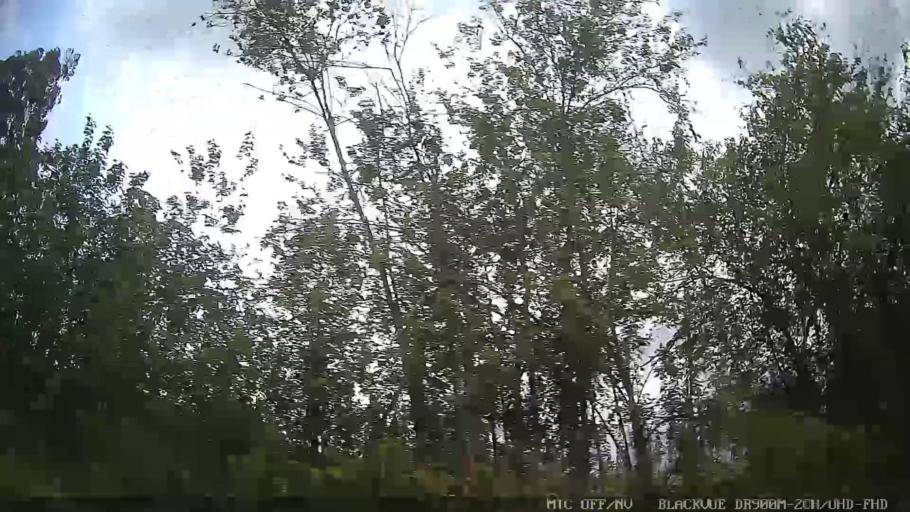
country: BR
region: Sao Paulo
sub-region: Amparo
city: Amparo
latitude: -22.8213
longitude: -46.7601
